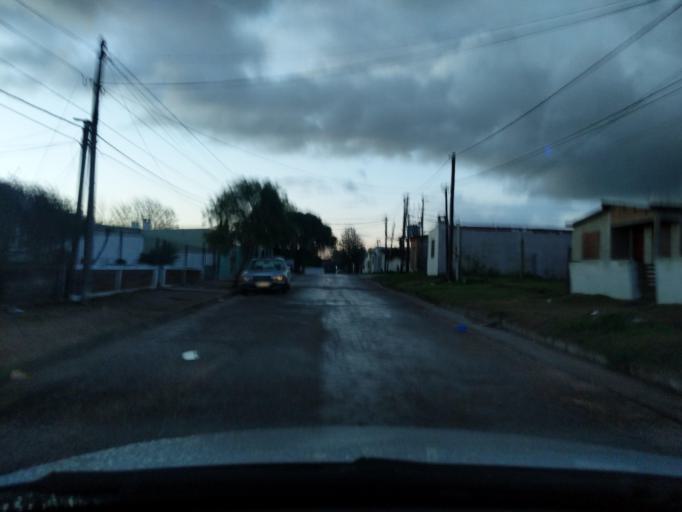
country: UY
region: Florida
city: Florida
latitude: -34.1089
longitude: -56.2110
